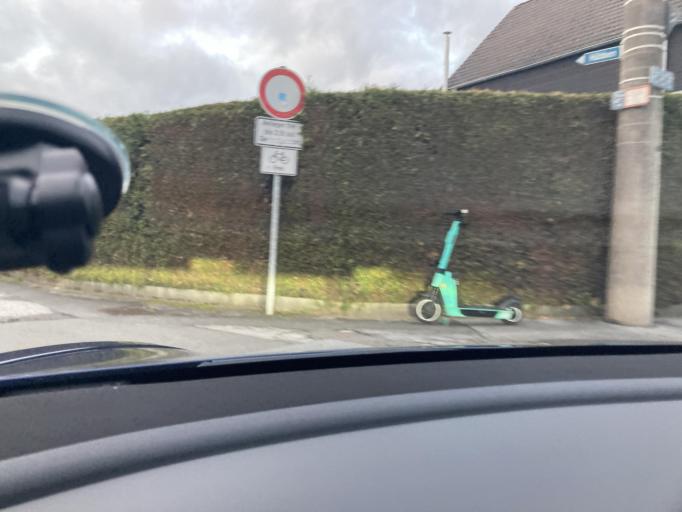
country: DE
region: North Rhine-Westphalia
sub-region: Regierungsbezirk Dusseldorf
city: Solingen
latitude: 51.1647
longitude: 7.0444
